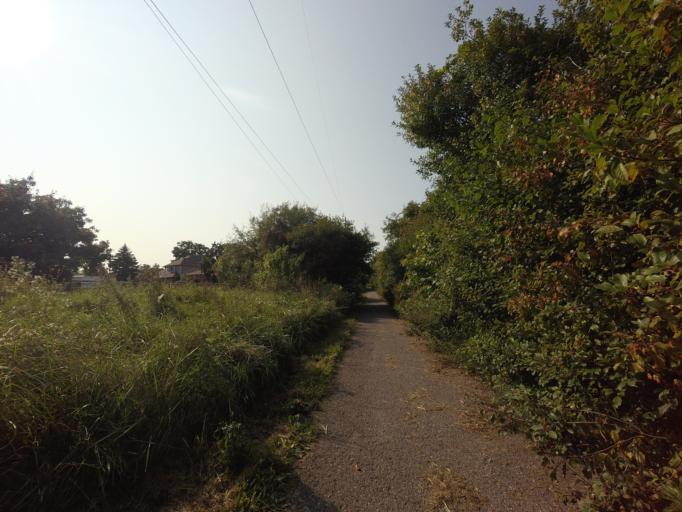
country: CA
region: Ontario
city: Bells Corners
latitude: 45.2909
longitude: -75.8471
